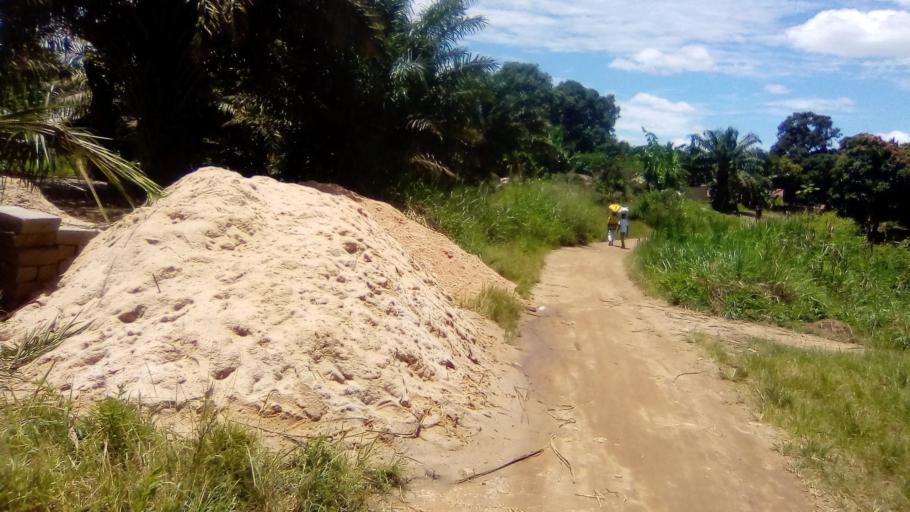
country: SL
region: Eastern Province
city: Simbakoro
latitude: 8.6251
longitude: -10.9884
